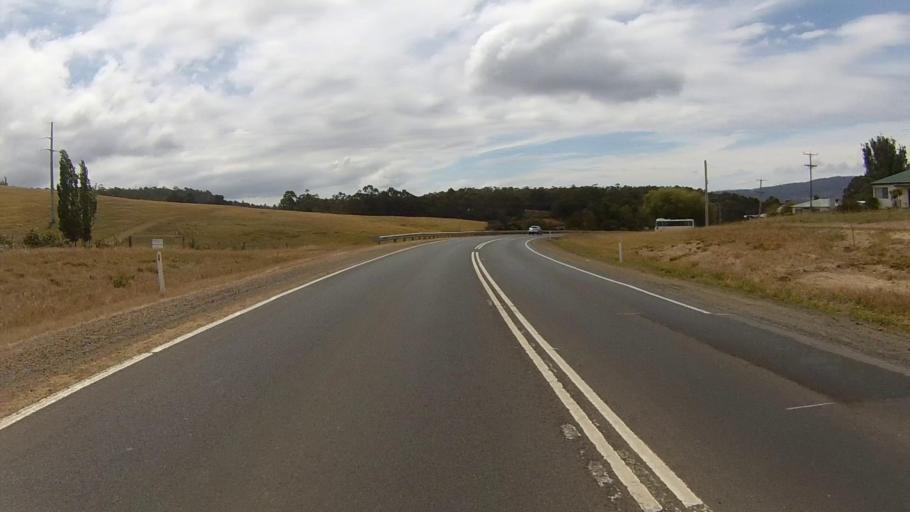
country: AU
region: Tasmania
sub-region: Kingborough
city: Margate
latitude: -43.0579
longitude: 147.2550
